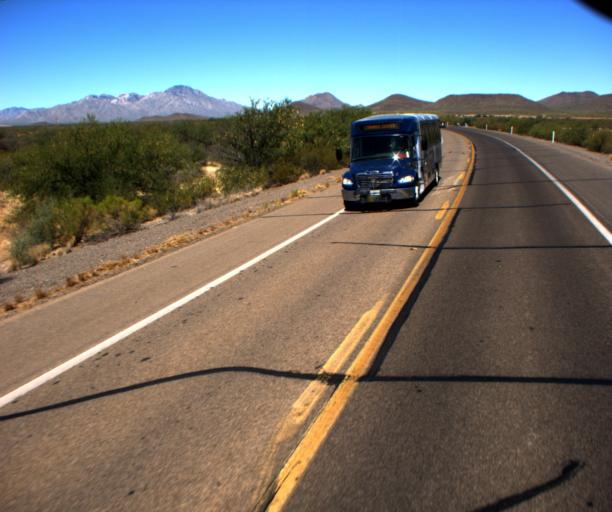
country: US
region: Arizona
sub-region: Pima County
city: Three Points
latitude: 32.0761
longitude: -111.3418
